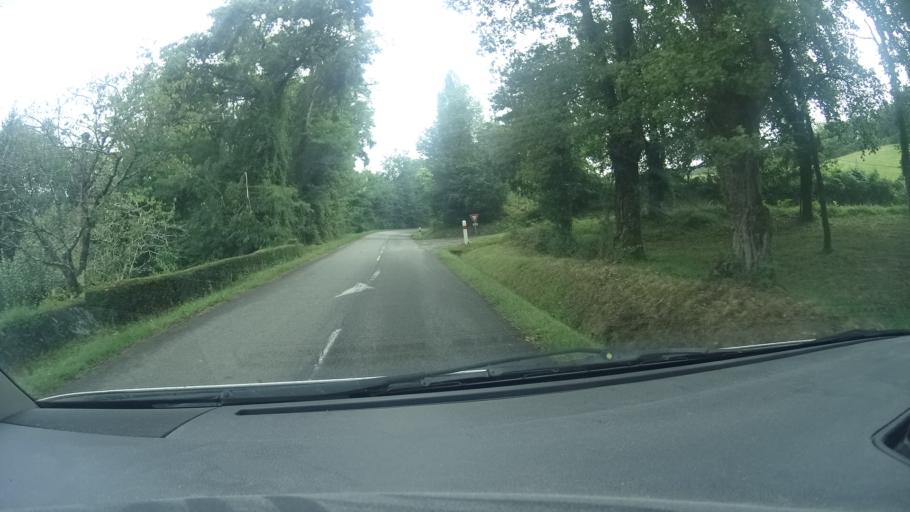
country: FR
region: Aquitaine
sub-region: Departement des Pyrenees-Atlantiques
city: Mont
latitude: 43.4864
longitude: -0.6947
